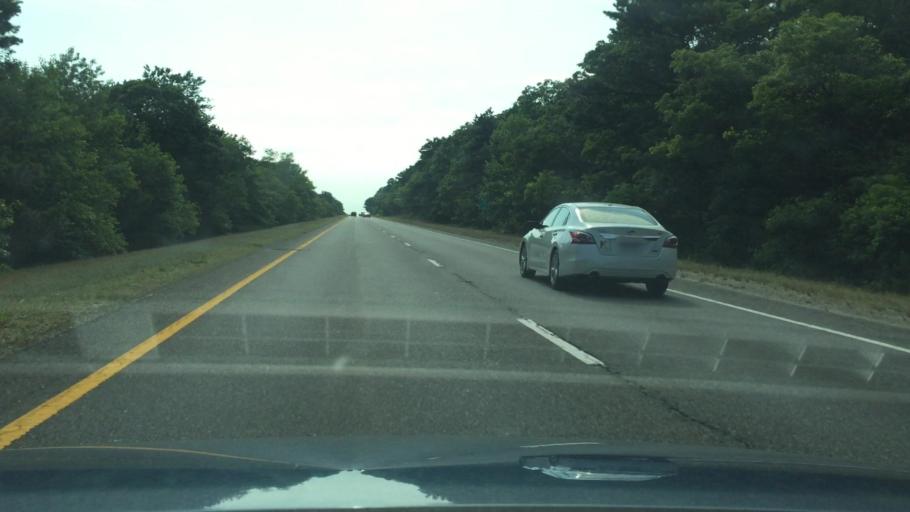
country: US
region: Massachusetts
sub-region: Barnstable County
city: Yarmouth
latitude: 41.6910
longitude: -70.2027
